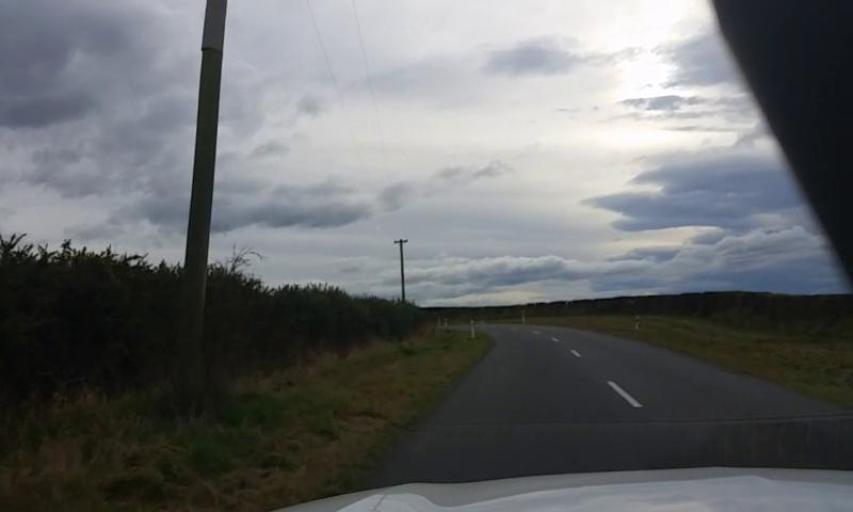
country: NZ
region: Canterbury
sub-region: Waimakariri District
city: Kaiapoi
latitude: -43.2964
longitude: 172.4373
